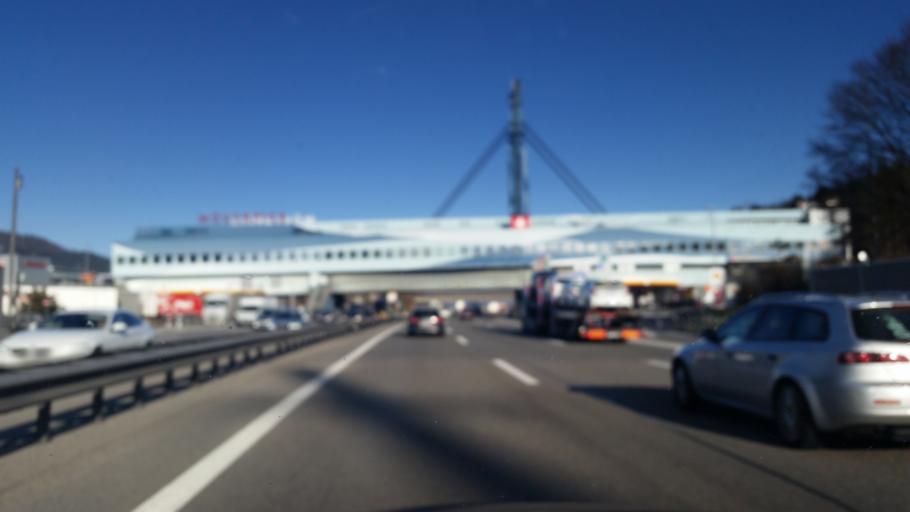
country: CH
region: Aargau
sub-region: Bezirk Baden
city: Killwangen
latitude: 47.4376
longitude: 8.3488
